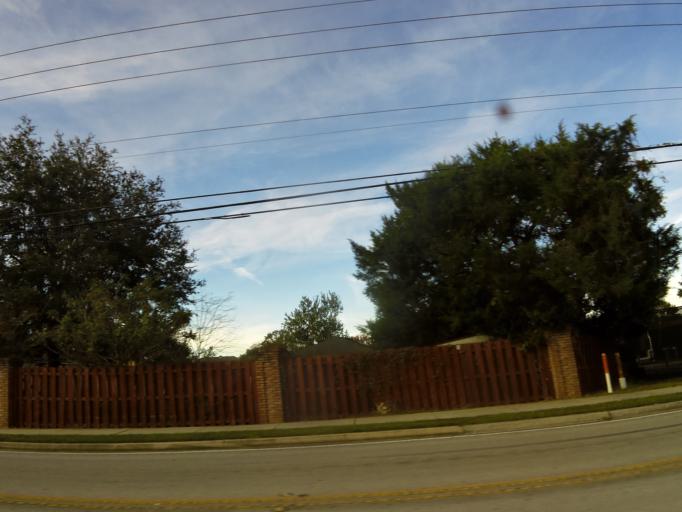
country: US
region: Florida
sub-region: Saint Johns County
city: Fruit Cove
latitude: 30.1613
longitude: -81.5863
